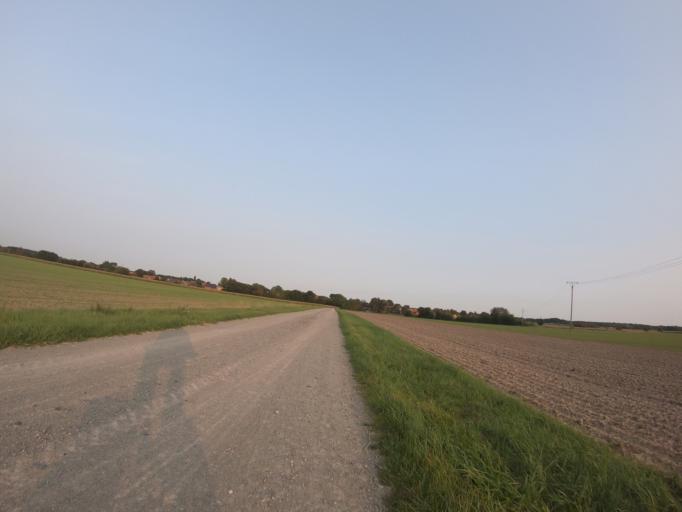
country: DE
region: Lower Saxony
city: Ribbesbuttel
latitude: 52.4269
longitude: 10.4756
